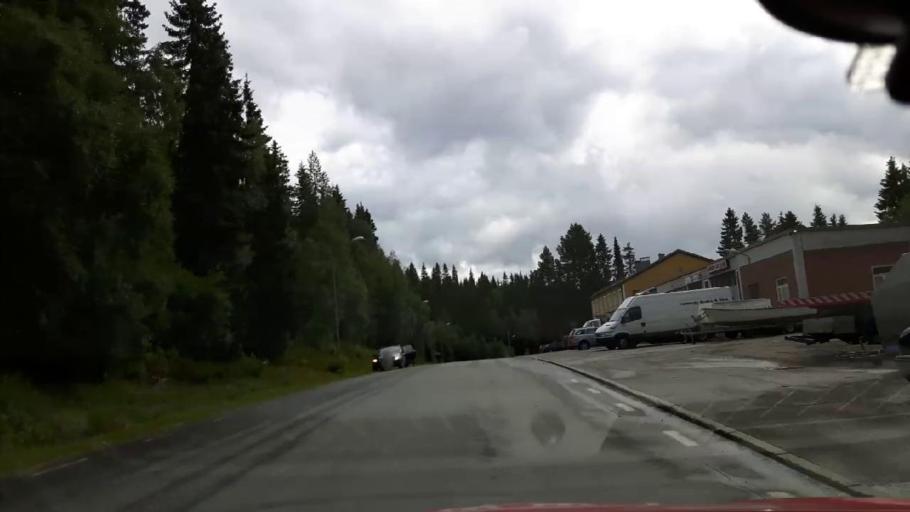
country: NO
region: Nord-Trondelag
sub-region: Lierne
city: Sandvika
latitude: 64.4968
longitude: 14.1488
